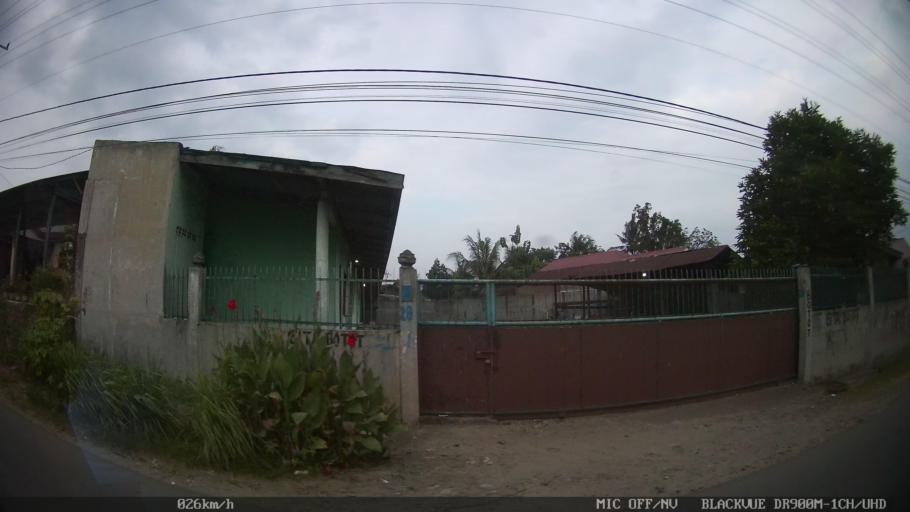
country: ID
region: North Sumatra
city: Sunggal
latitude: 3.5711
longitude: 98.5832
